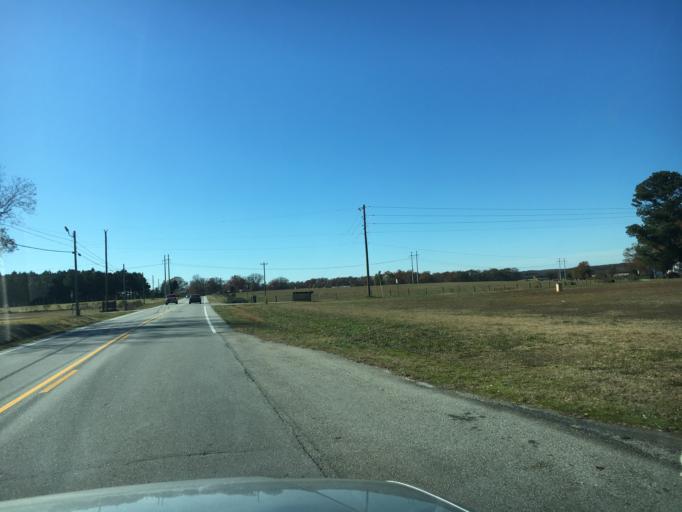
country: US
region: Georgia
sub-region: Hart County
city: Hartwell
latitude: 34.3178
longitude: -82.9869
